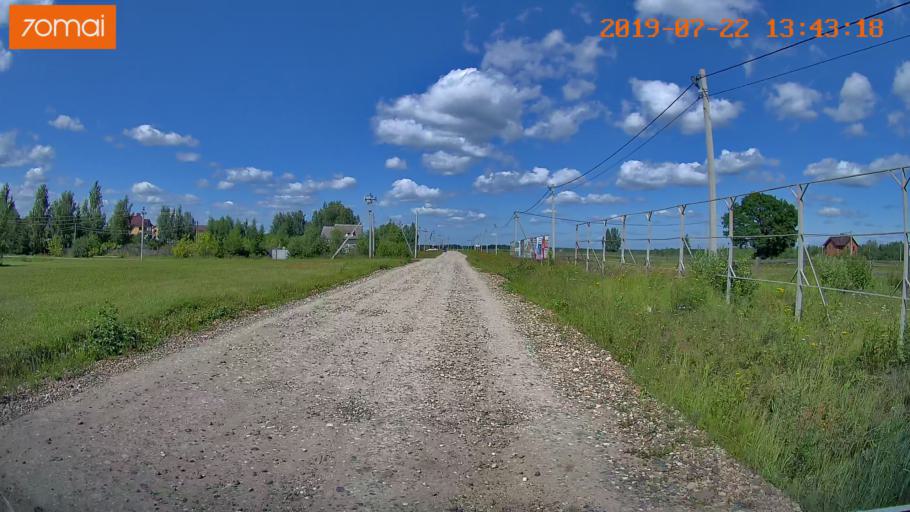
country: RU
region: Ivanovo
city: Novo-Talitsy
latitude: 57.0825
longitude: 40.8743
